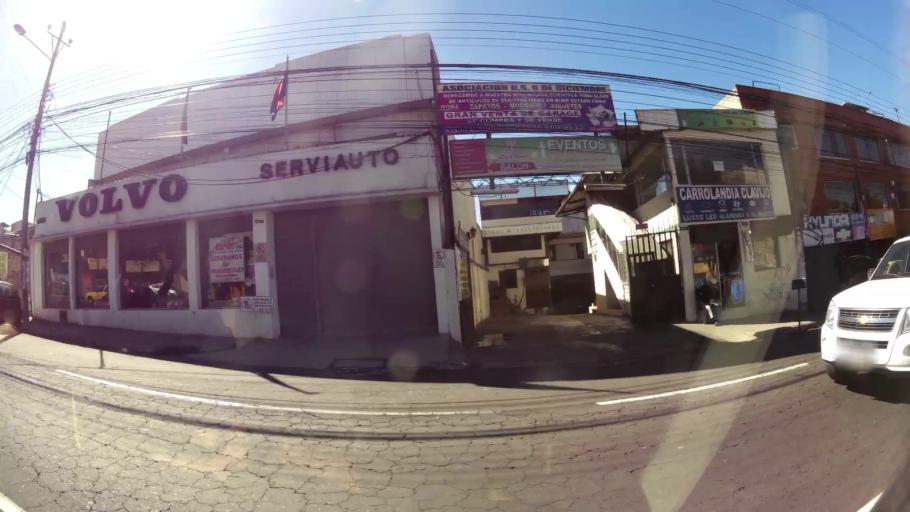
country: EC
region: Pichincha
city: Quito
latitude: -0.1474
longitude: -78.4752
